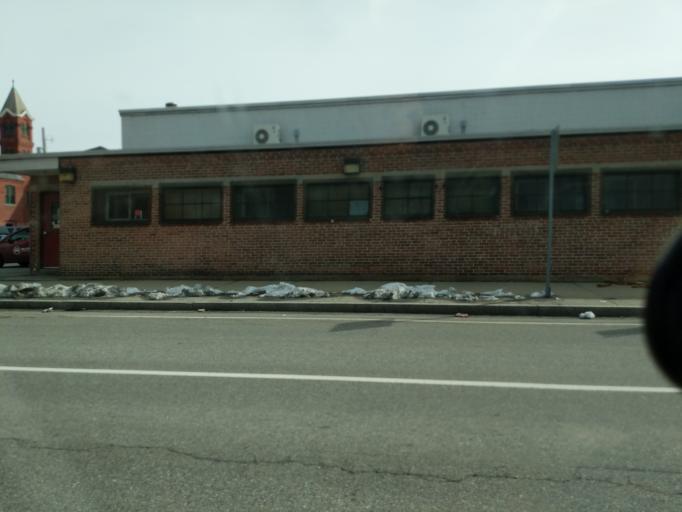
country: US
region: Massachusetts
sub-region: Worcester County
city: Worcester
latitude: 42.2435
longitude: -71.8094
